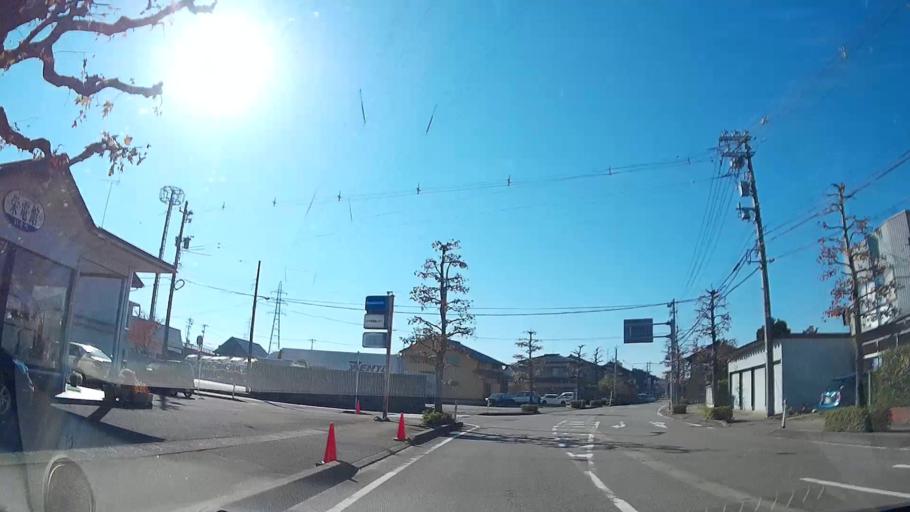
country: JP
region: Toyama
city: Nanto-shi
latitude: 36.6450
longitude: 136.9592
